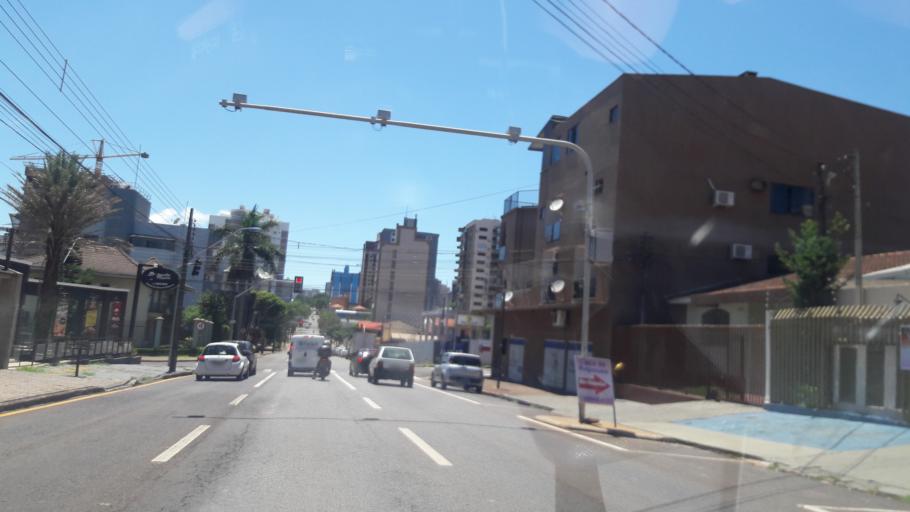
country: BR
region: Parana
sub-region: Cascavel
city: Cascavel
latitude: -24.9515
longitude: -53.4706
